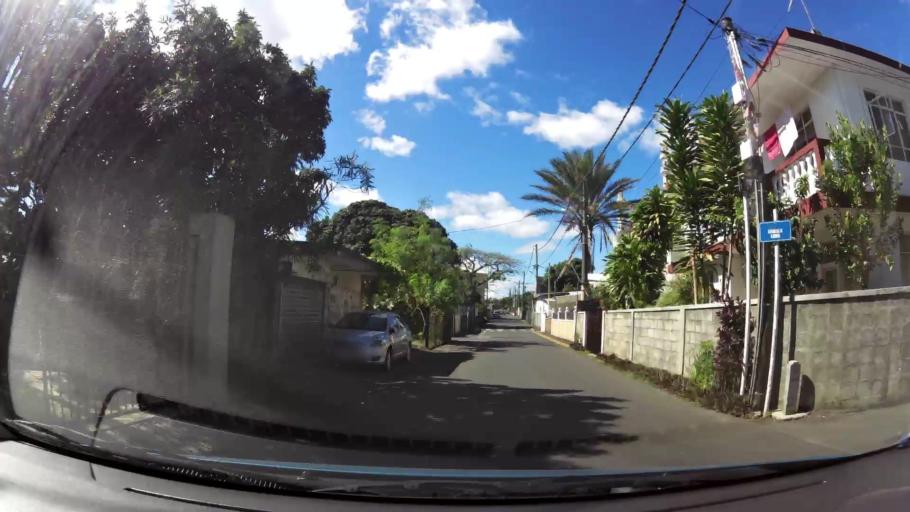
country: MU
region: Plaines Wilhems
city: Vacoas
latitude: -20.3085
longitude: 57.4822
